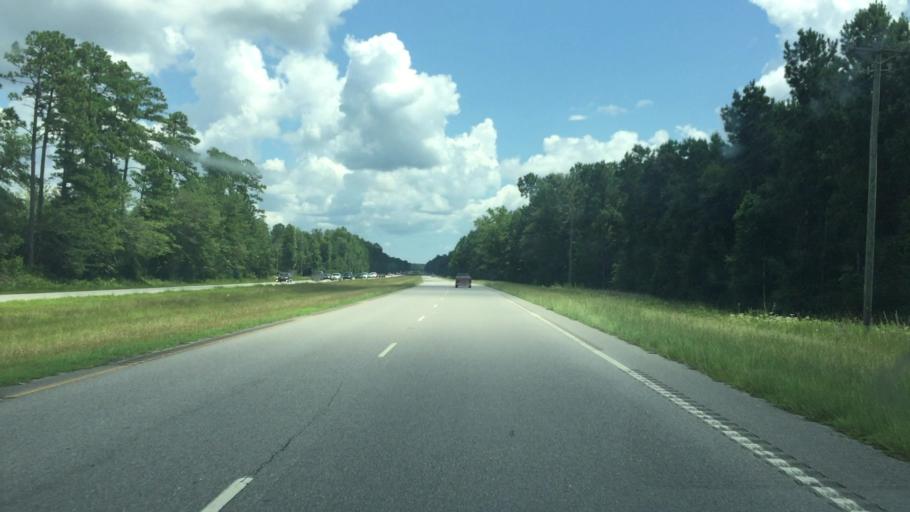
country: US
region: South Carolina
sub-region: Horry County
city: Loris
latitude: 34.0458
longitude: -78.8310
